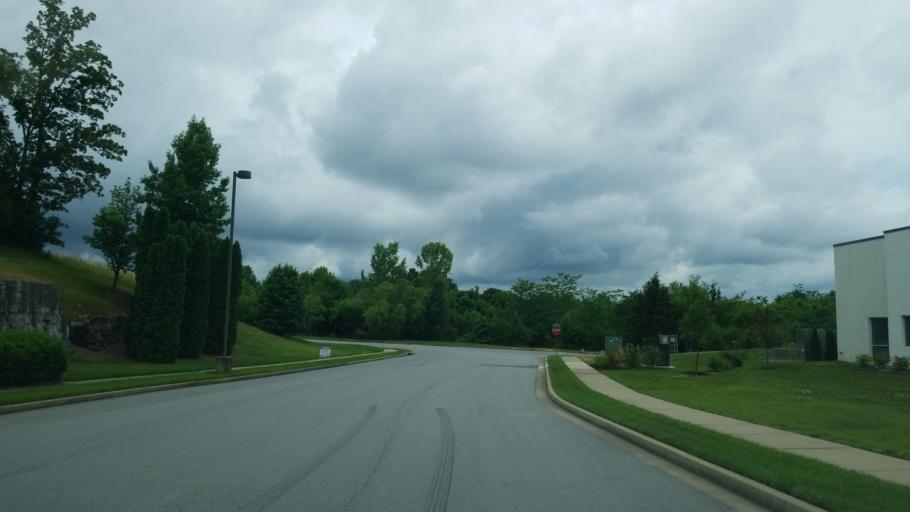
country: US
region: Tennessee
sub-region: Rutherford County
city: La Vergne
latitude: 36.1090
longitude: -86.6420
